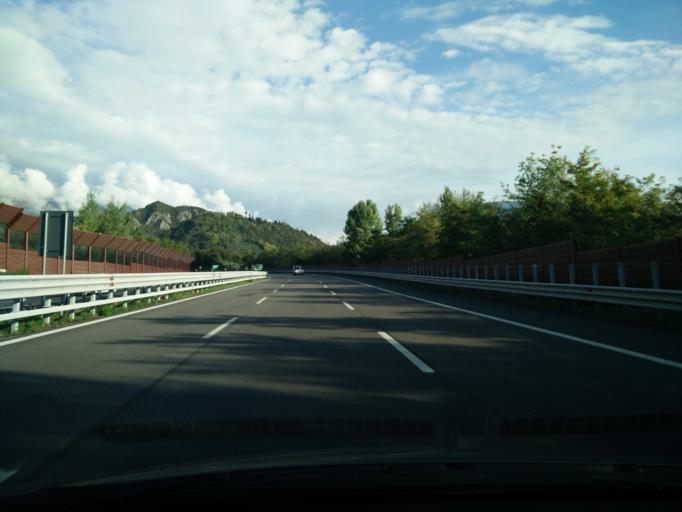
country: IT
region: Veneto
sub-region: Provincia di Treviso
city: Carpesica
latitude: 45.9679
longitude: 12.2867
